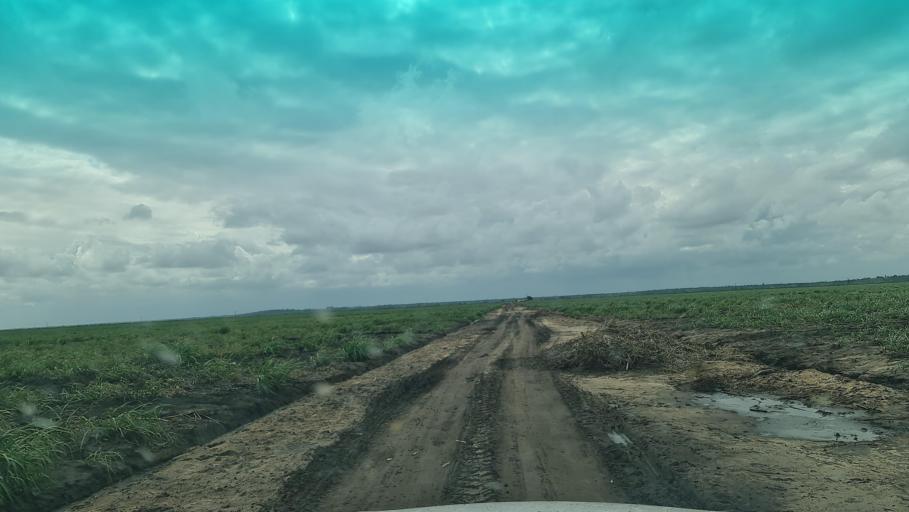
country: MZ
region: Maputo
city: Manhica
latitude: -25.4384
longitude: 32.8496
